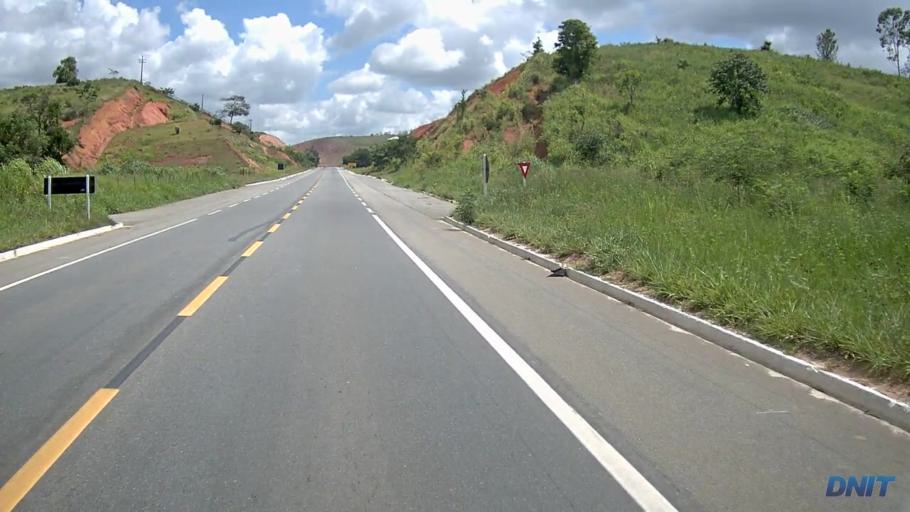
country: BR
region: Minas Gerais
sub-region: Governador Valadares
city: Governador Valadares
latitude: -18.9015
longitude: -42.0037
